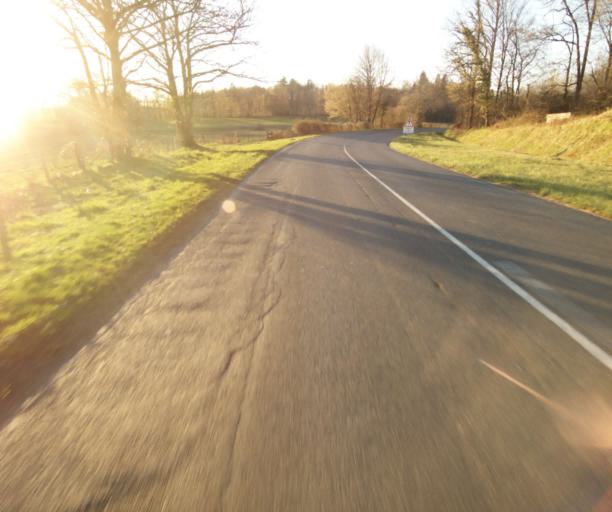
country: FR
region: Limousin
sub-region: Departement de la Correze
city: Saint-Clement
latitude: 45.3321
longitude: 1.6804
